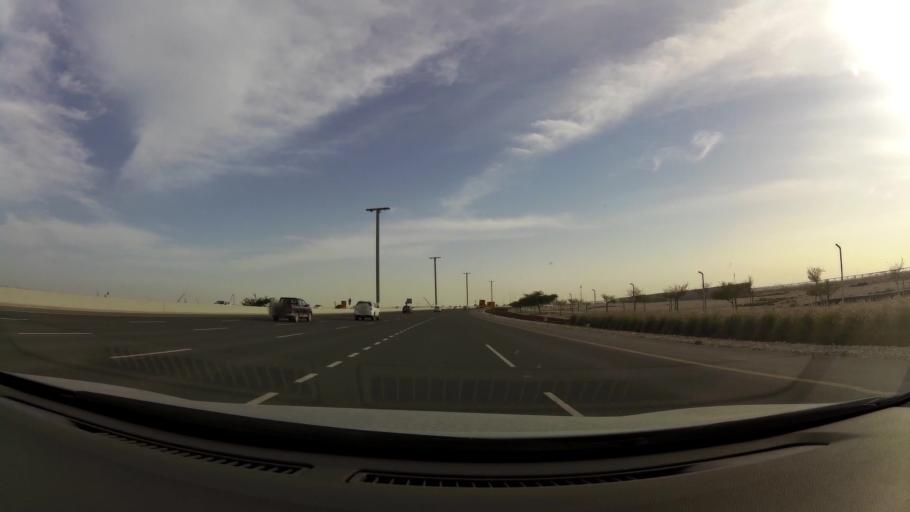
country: QA
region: Al Wakrah
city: Al Wakrah
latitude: 25.2327
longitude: 51.5927
